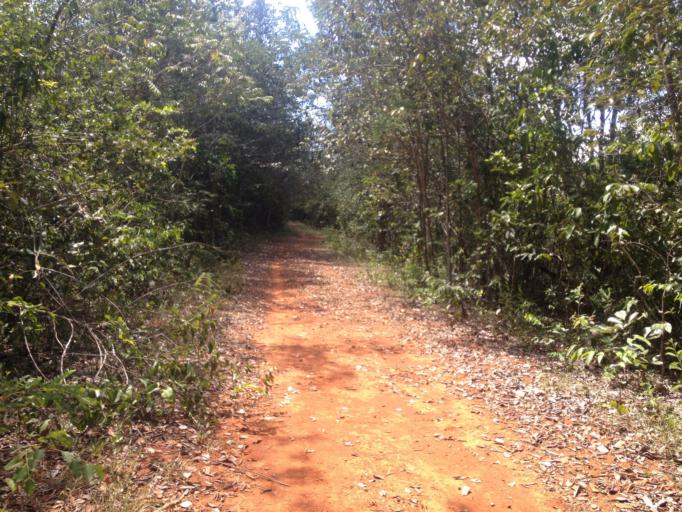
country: BR
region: Minas Gerais
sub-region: Unai
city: Unai
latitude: -16.1262
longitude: -47.3642
